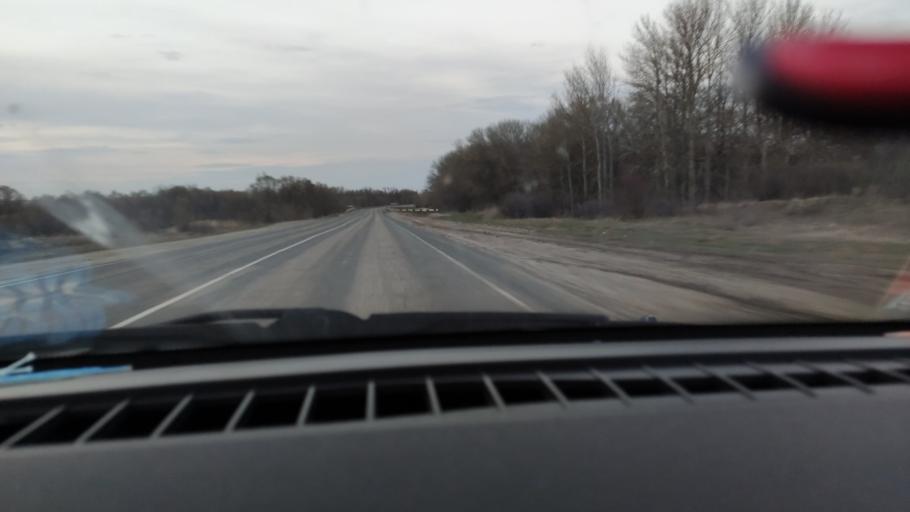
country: RU
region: Saratov
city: Sinodskoye
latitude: 51.9782
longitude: 46.6513
